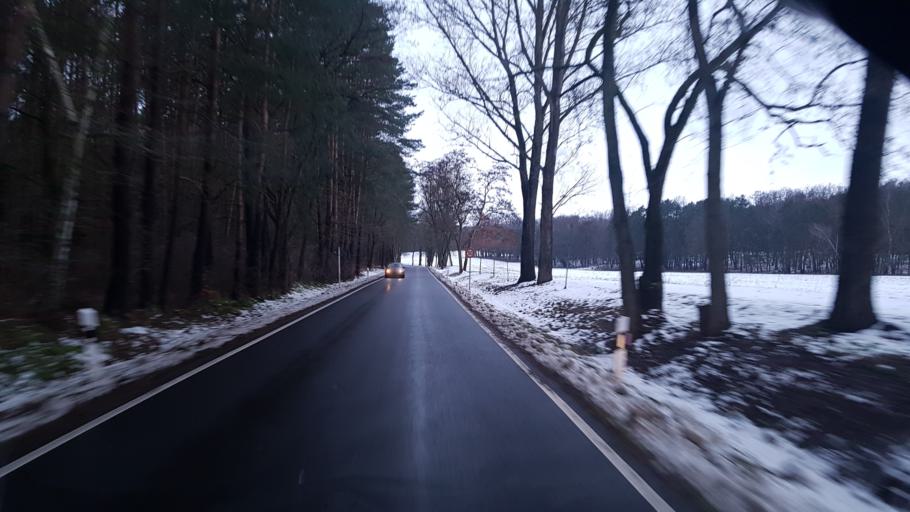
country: DE
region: Brandenburg
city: Gross Lindow
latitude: 52.2799
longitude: 14.5258
